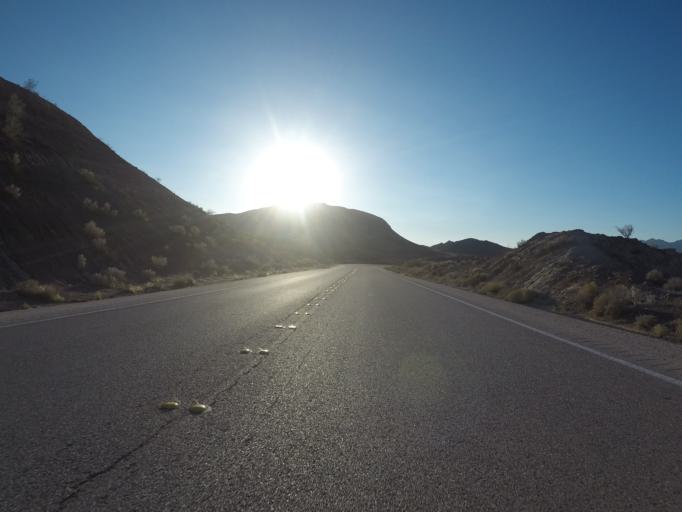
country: US
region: Nevada
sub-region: Clark County
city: Moapa Valley
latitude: 36.2432
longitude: -114.5384
